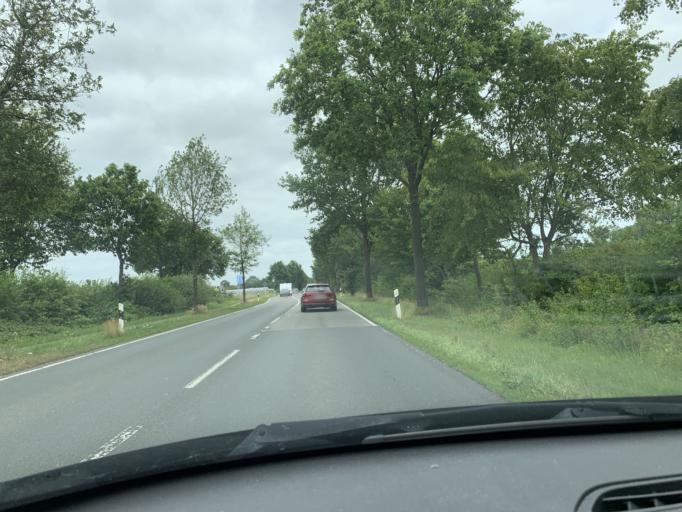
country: DE
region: Lower Saxony
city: Westerstede
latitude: 53.2700
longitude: 7.9513
